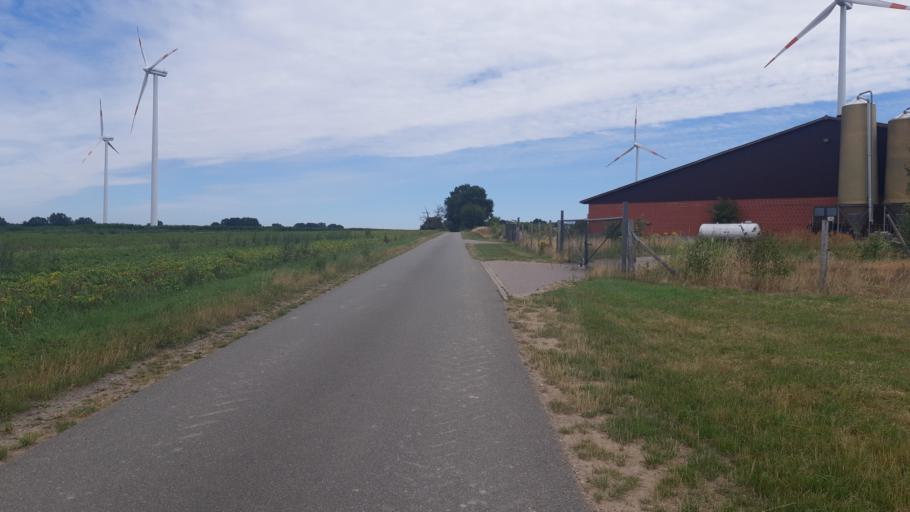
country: DE
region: Lower Saxony
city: Dahlem
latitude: 53.2222
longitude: 10.7681
